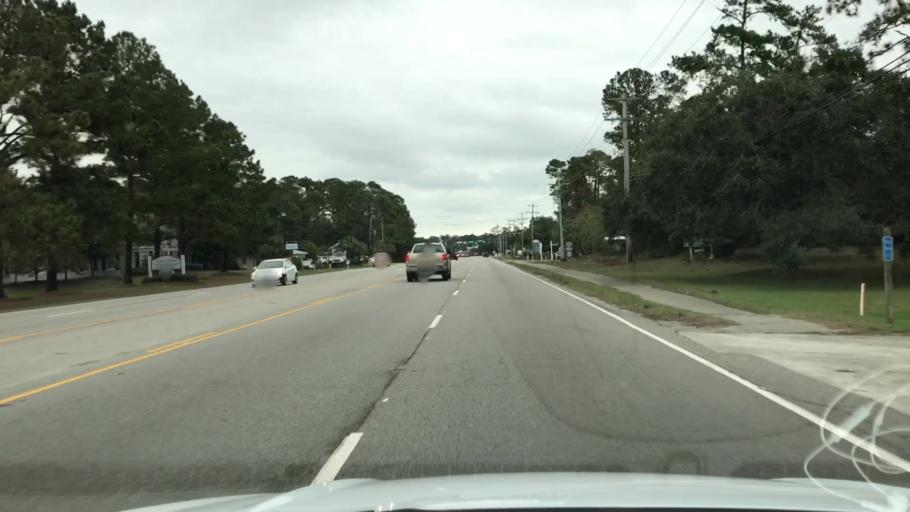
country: US
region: South Carolina
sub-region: Georgetown County
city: Murrells Inlet
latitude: 33.4346
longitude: -79.1355
